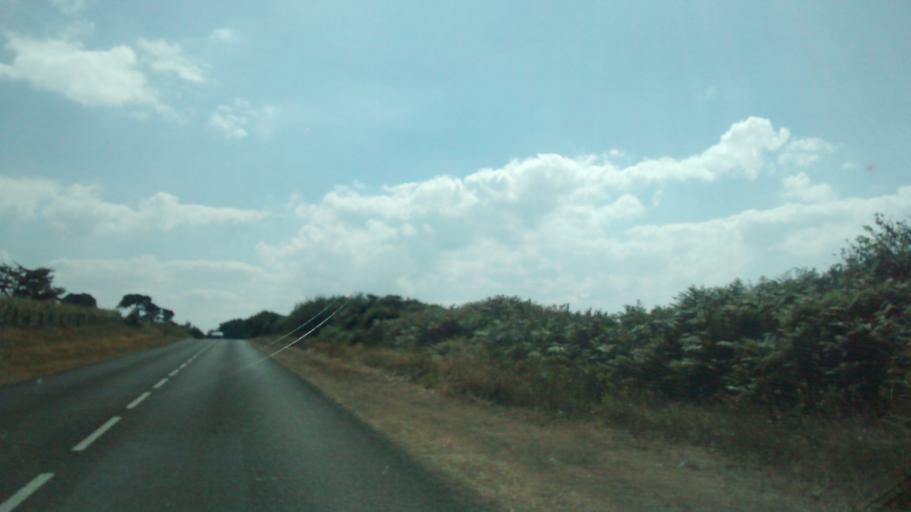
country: FR
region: Brittany
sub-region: Departement d'Ille-et-Vilaine
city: Cancale
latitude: 48.6990
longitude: -1.8603
